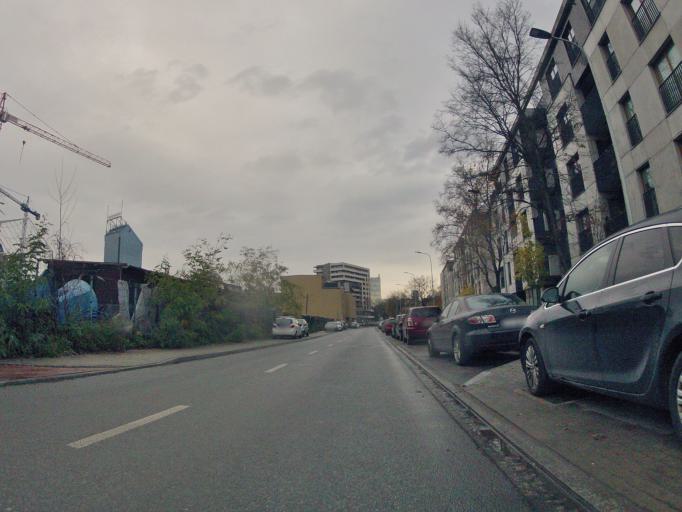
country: PL
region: Lesser Poland Voivodeship
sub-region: Krakow
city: Krakow
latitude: 50.0557
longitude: 19.9650
